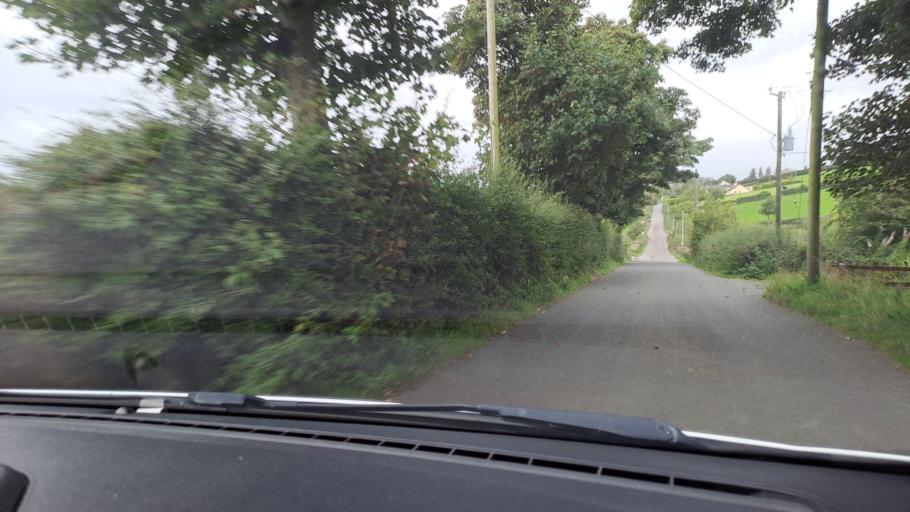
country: IE
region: Ulster
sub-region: An Cabhan
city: Kingscourt
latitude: 54.0072
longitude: -6.8133
